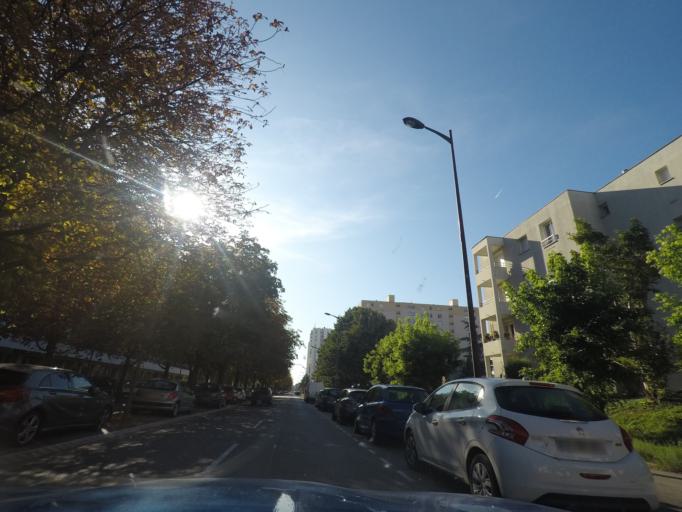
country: FR
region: Lorraine
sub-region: Departement de la Moselle
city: Thionville
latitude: 49.3643
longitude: 6.1532
